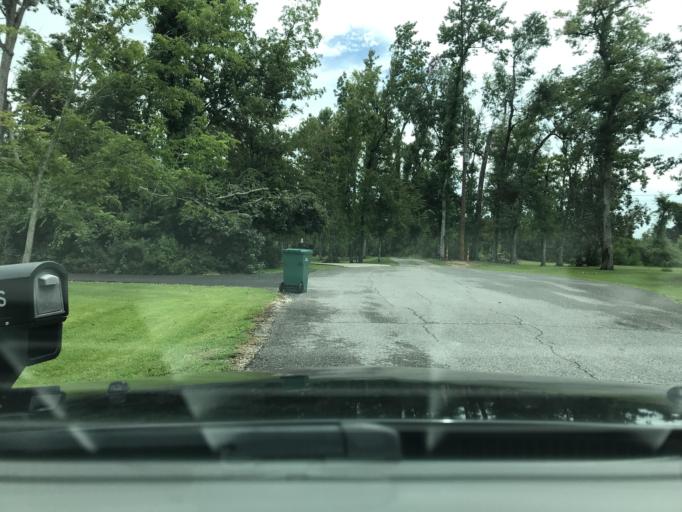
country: US
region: Louisiana
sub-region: Calcasieu Parish
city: Moss Bluff
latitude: 30.3108
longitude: -93.1818
